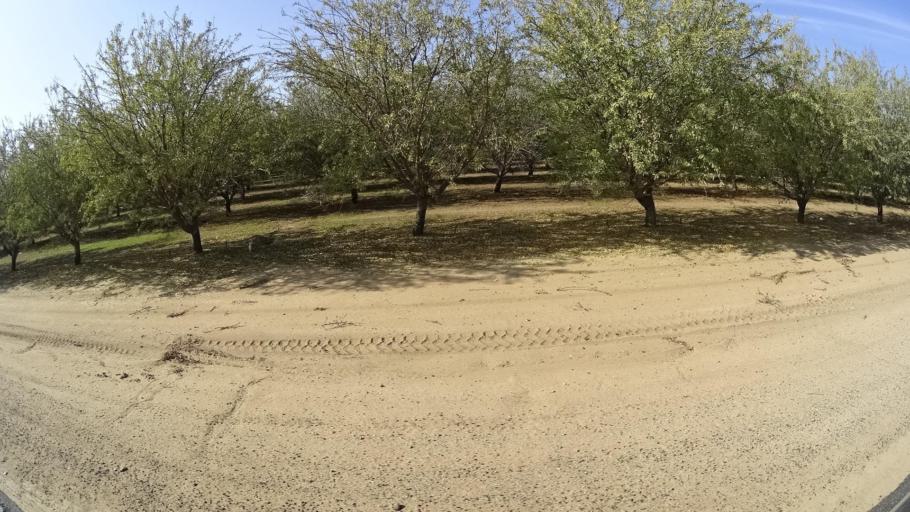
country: US
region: California
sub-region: Kern County
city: Shafter
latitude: 35.5242
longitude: -119.1517
